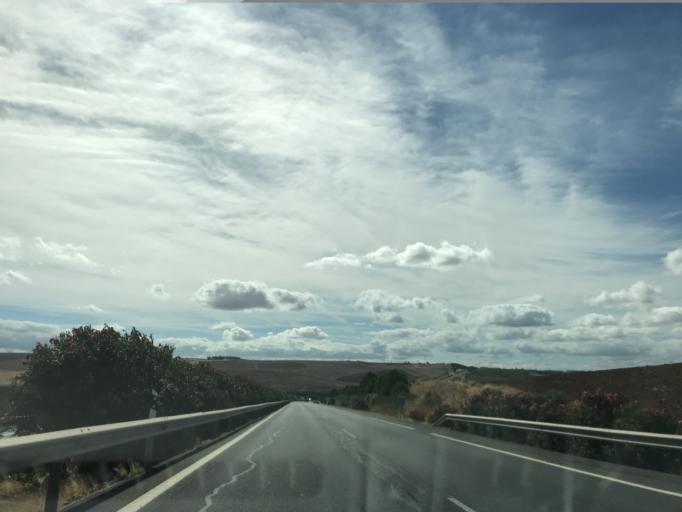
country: ES
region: Andalusia
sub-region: Province of Cordoba
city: La Victoria
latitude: 37.7416
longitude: -4.8497
